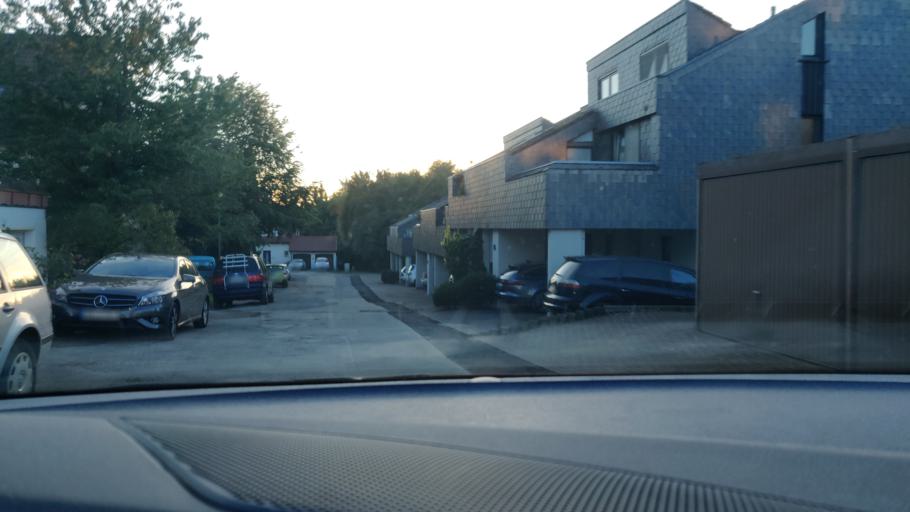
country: DE
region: North Rhine-Westphalia
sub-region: Regierungsbezirk Dusseldorf
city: Velbert
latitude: 51.3136
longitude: 7.0599
